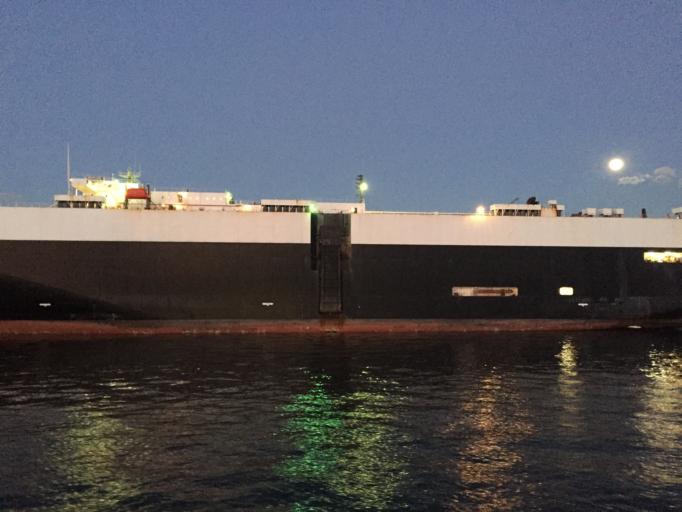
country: JP
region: Kanagawa
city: Yokohama
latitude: 35.4637
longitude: 139.6501
